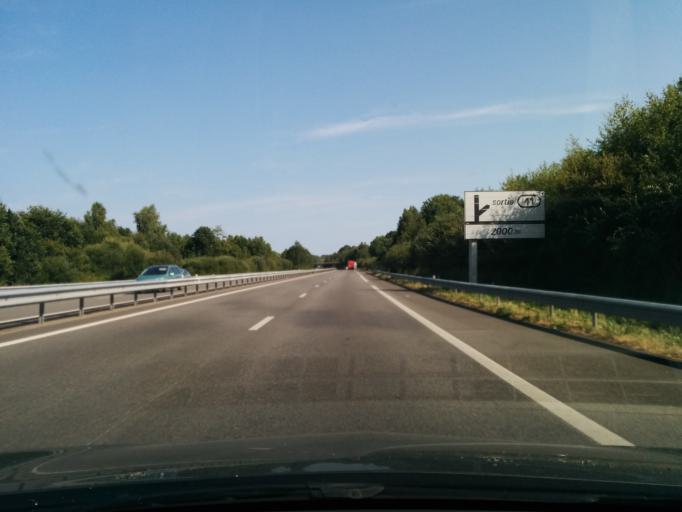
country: FR
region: Limousin
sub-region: Departement de la Haute-Vienne
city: Vicq-sur-Breuilh
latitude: 45.6387
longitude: 1.4221
